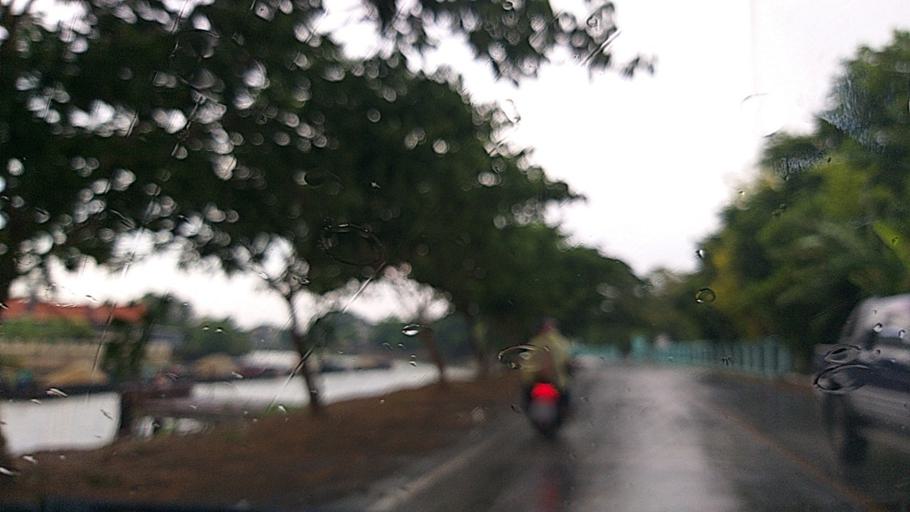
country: TH
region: Phra Nakhon Si Ayutthaya
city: Phra Nakhon Si Ayutthaya
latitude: 14.3533
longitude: 100.5475
